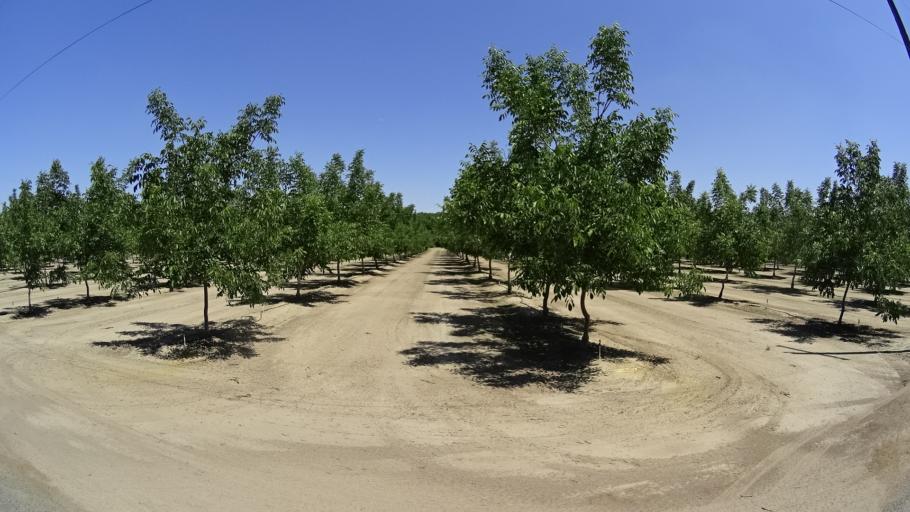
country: US
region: California
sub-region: Kings County
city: Lucerne
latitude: 36.3956
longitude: -119.6550
